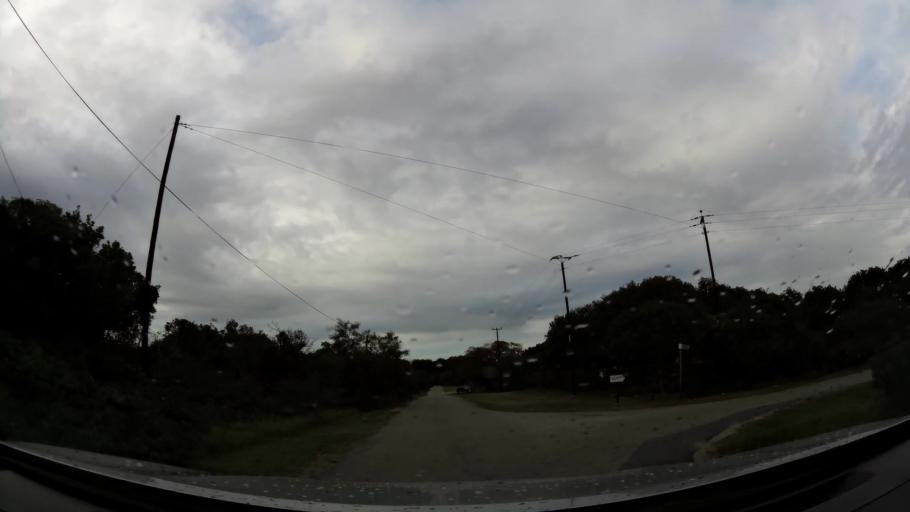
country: ZA
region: Eastern Cape
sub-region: Nelson Mandela Bay Metropolitan Municipality
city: Port Elizabeth
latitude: -34.0185
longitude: 25.5102
